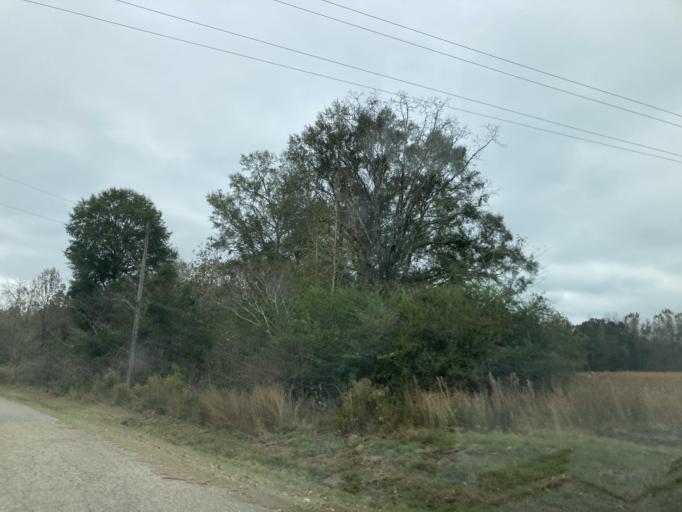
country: US
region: Mississippi
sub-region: Lamar County
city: Purvis
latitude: 31.2480
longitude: -89.4972
